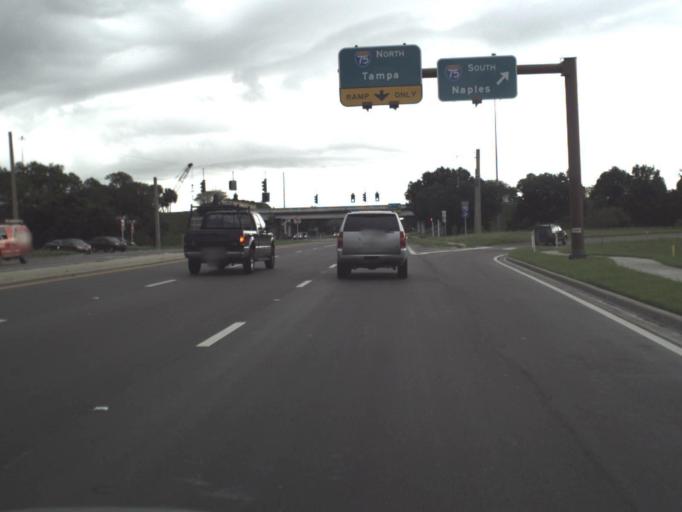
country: US
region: Florida
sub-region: Sarasota County
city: Lake Sarasota
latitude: 27.2987
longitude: -82.4507
